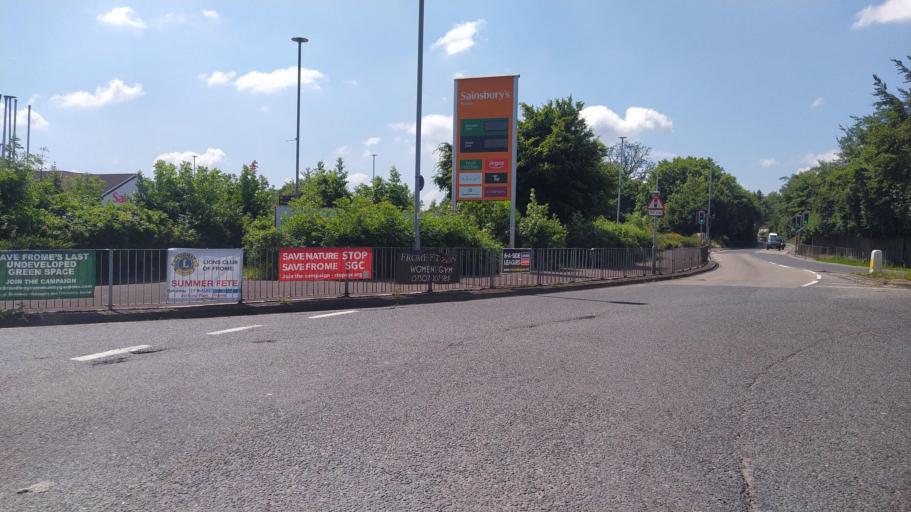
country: GB
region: England
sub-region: Somerset
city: Frome
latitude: 51.2171
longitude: -2.3339
